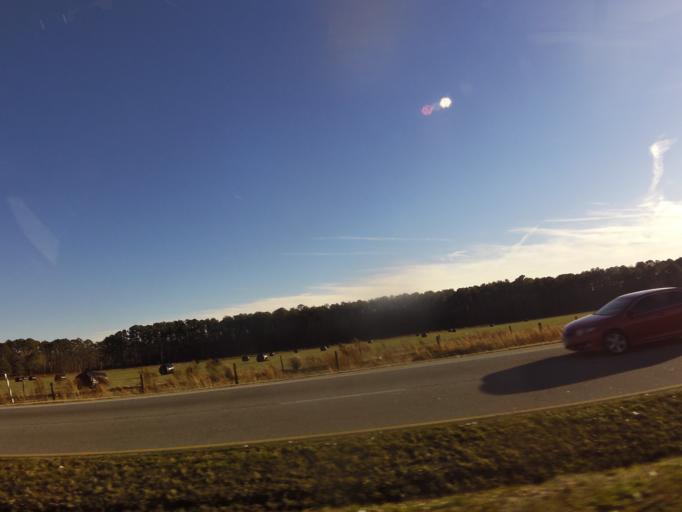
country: US
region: Virginia
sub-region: Isle of Wight County
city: Windsor
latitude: 36.6946
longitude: -76.7193
